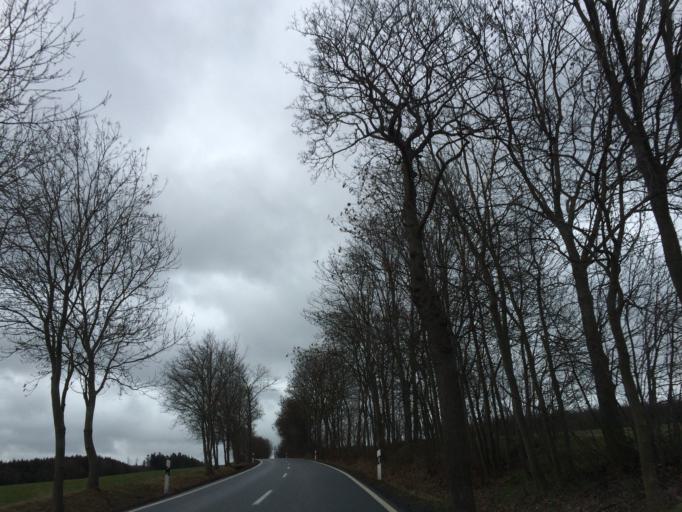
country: DE
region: Thuringia
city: Bodelwitz
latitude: 50.6680
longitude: 11.6188
